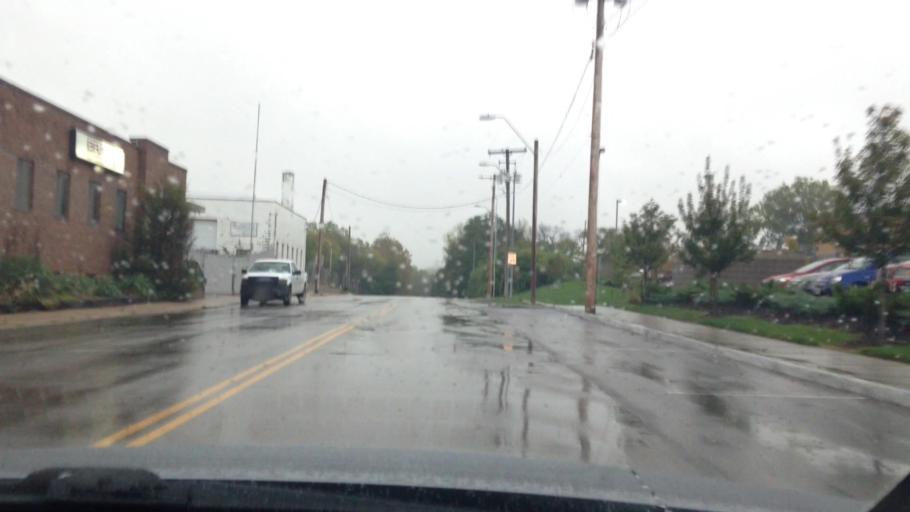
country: US
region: Missouri
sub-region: Jackson County
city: Kansas City
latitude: 39.1114
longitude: -94.5758
